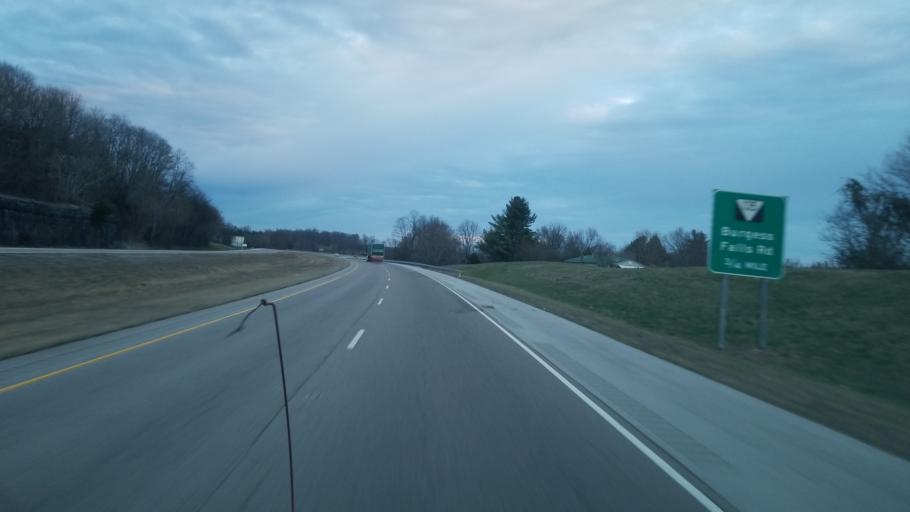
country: US
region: Tennessee
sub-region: White County
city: Sparta
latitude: 35.9786
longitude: -85.4927
